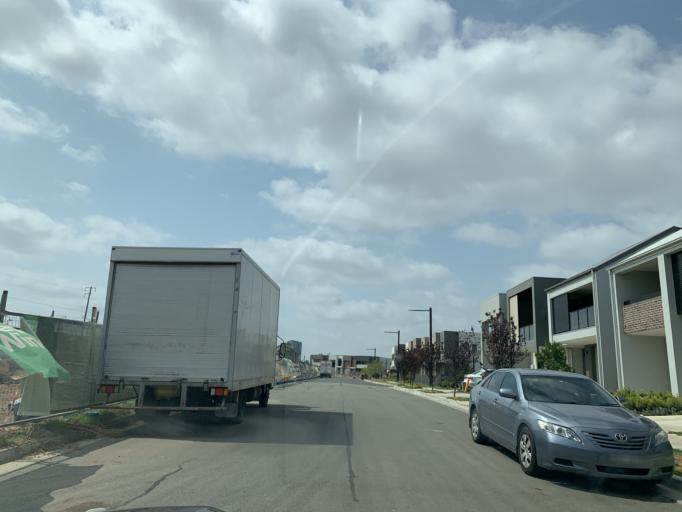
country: AU
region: New South Wales
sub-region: Blacktown
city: Blacktown
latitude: -33.7568
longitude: 150.9032
